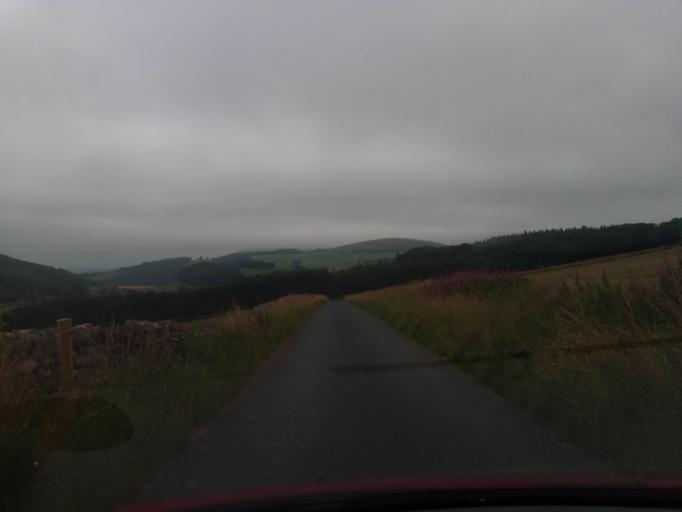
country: GB
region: Scotland
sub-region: The Scottish Borders
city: Galashiels
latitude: 55.6589
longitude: -2.8757
